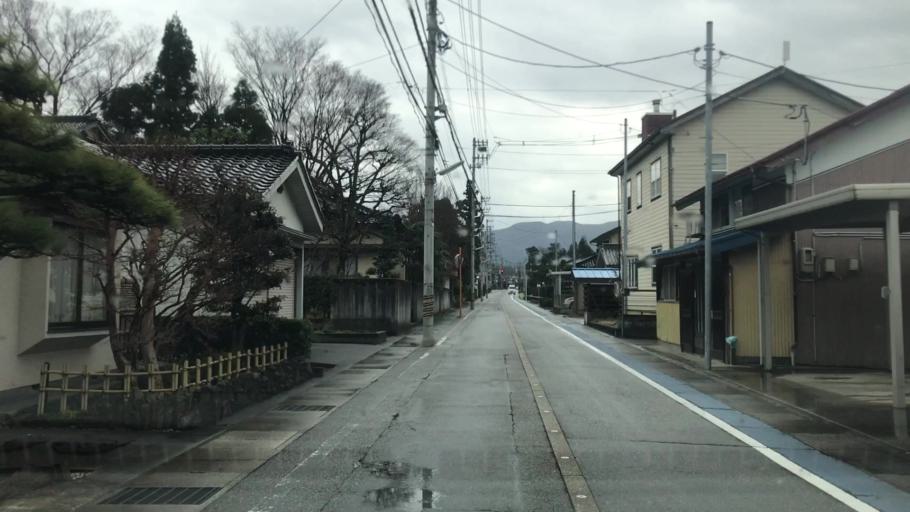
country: JP
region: Toyama
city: Yatsuomachi-higashikumisaka
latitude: 36.5946
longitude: 137.2065
